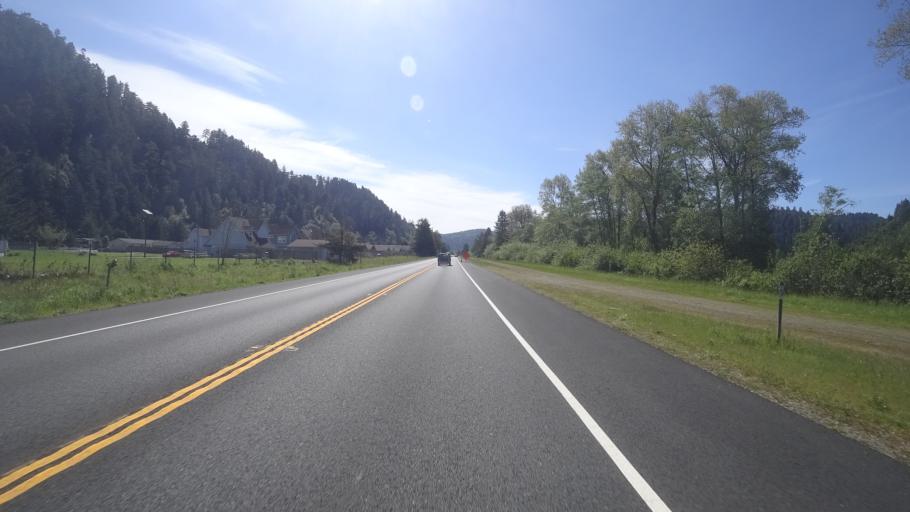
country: US
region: California
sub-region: Del Norte County
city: Bertsch-Oceanview
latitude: 41.5344
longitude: -124.0450
